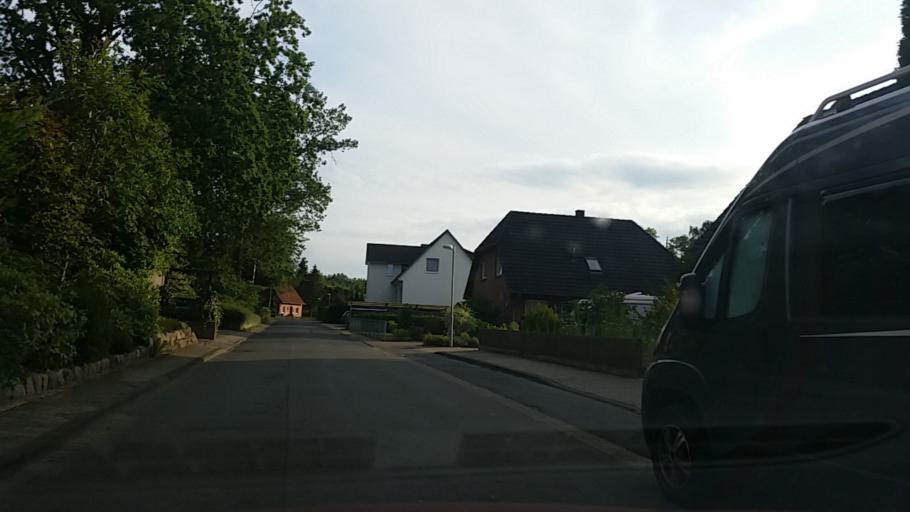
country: DE
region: Lower Saxony
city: Adendorf
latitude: 53.2592
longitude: 10.4706
